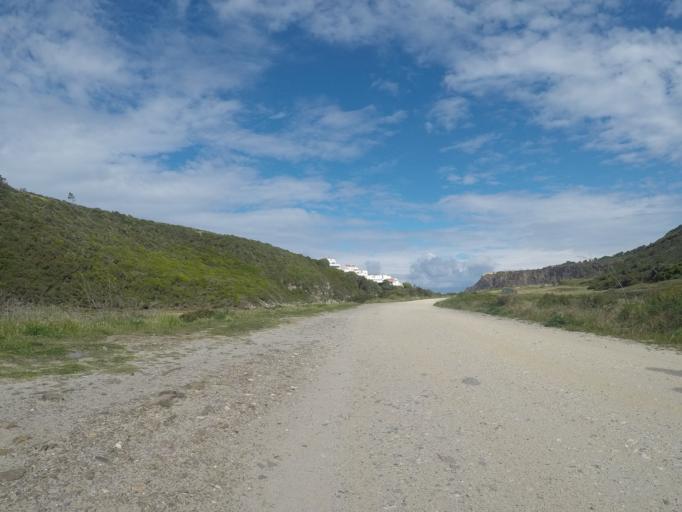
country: PT
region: Beja
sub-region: Odemira
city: Sao Teotonio
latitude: 37.4386
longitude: -8.7939
